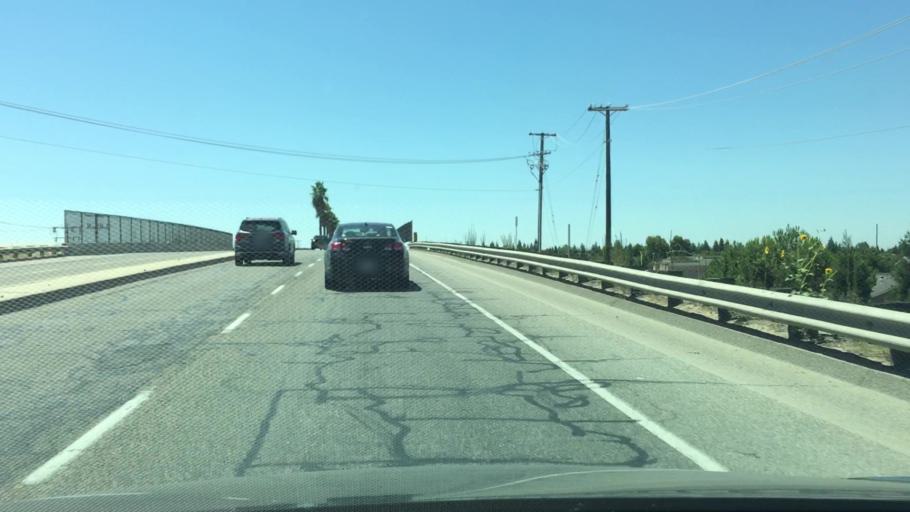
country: US
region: California
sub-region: Fresno County
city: West Park
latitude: 36.8371
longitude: -119.8847
